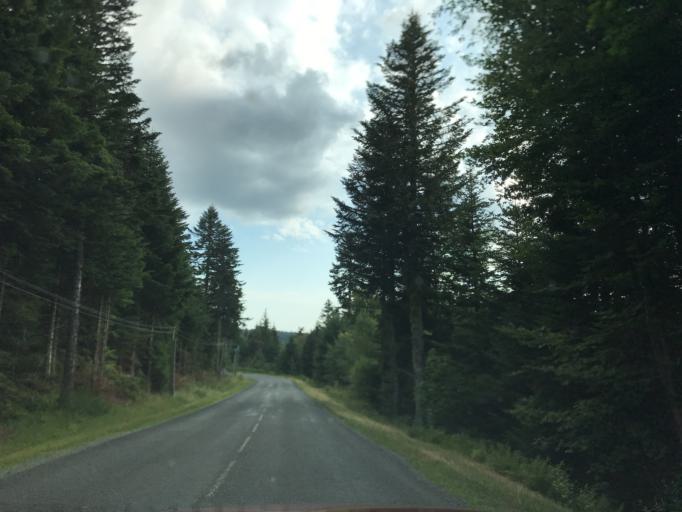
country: FR
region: Rhone-Alpes
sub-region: Departement de la Loire
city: Noiretable
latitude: 45.7636
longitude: 3.7370
